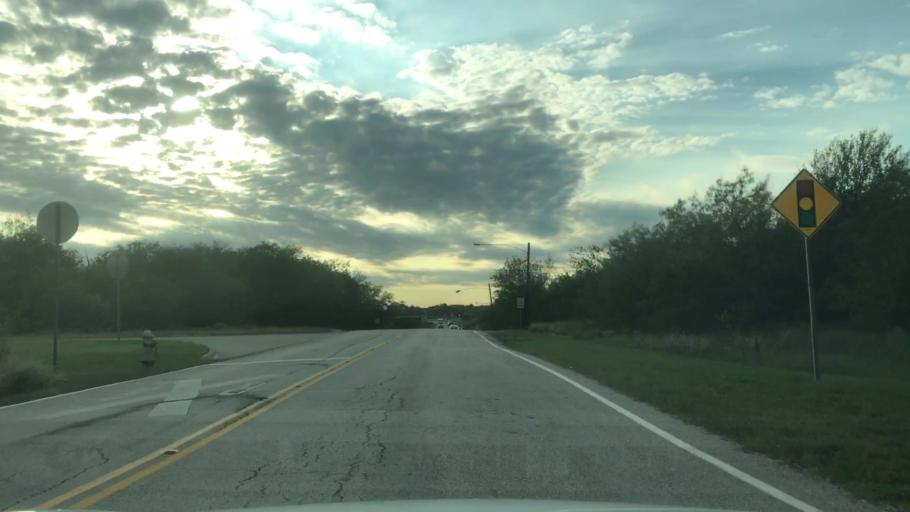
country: US
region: Texas
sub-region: Dallas County
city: Coppell
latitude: 32.8888
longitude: -96.9889
